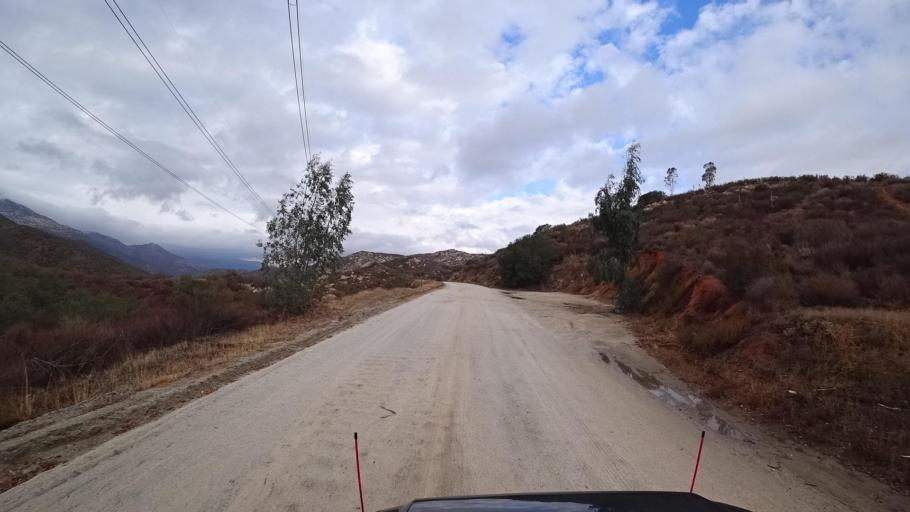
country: MX
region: Baja California
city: Tecate
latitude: 32.5973
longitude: -116.6376
